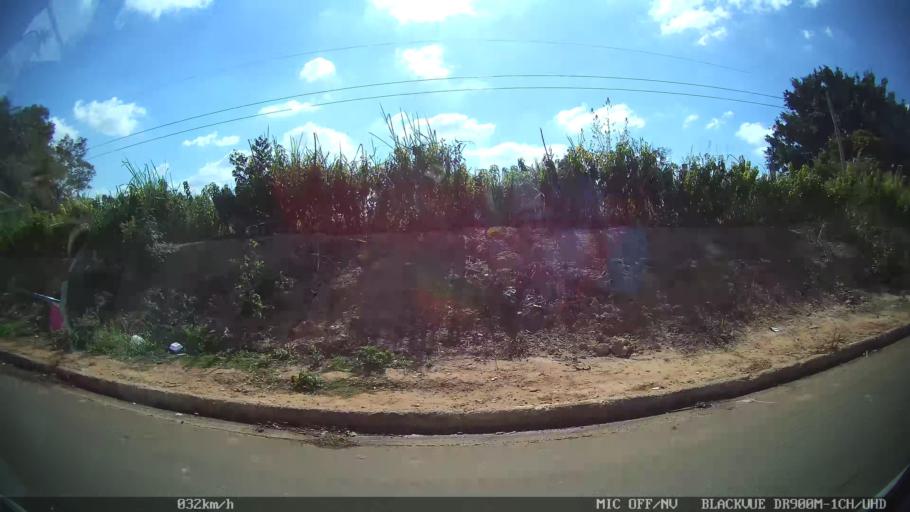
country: BR
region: Sao Paulo
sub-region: Hortolandia
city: Hortolandia
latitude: -22.8735
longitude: -47.2365
